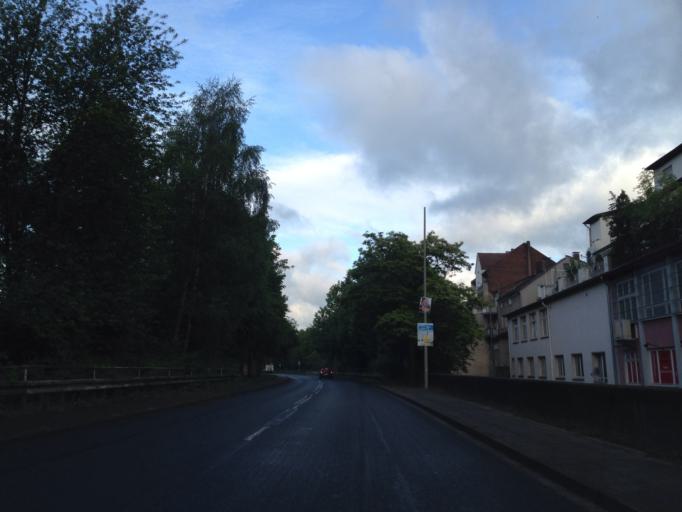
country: DE
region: North Rhine-Westphalia
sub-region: Regierungsbezirk Arnsberg
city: Nachrodt-Wiblingwerde
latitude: 51.3647
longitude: 7.6165
